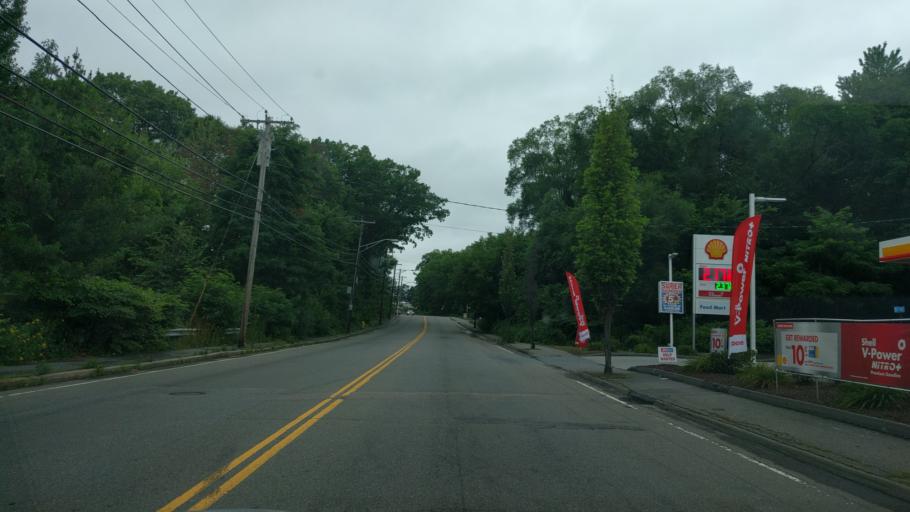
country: US
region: Massachusetts
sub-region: Worcester County
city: Sunderland
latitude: 42.2421
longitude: -71.7548
